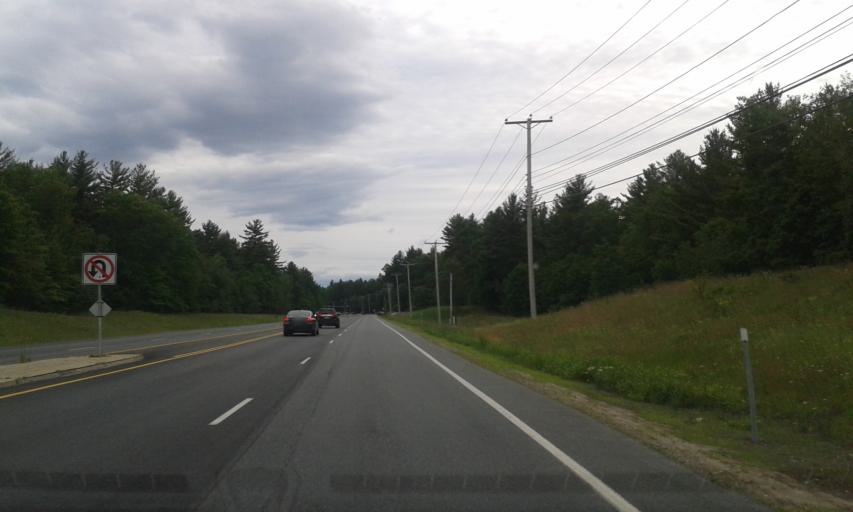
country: US
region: New Hampshire
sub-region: Hillsborough County
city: Litchfield
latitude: 42.8233
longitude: -71.5138
